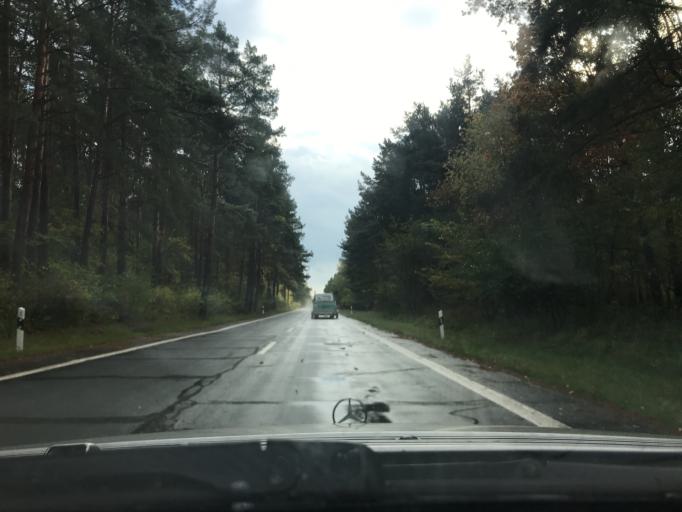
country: DE
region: Mecklenburg-Vorpommern
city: Karlshagen
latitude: 54.1241
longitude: 13.8252
